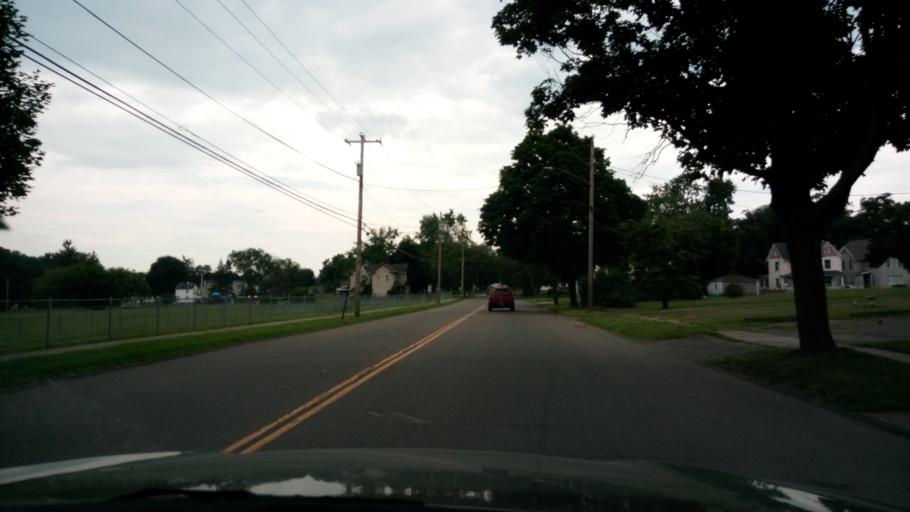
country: US
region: New York
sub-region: Chemung County
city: Elmira Heights
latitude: 42.1129
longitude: -76.8076
